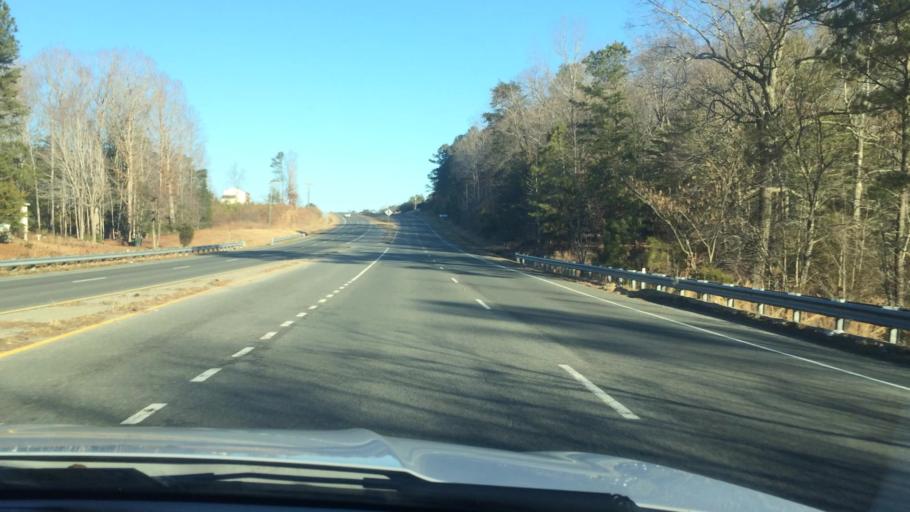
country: US
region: Virginia
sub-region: Lancaster County
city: Kilmarnock
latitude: 37.7325
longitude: -76.3915
